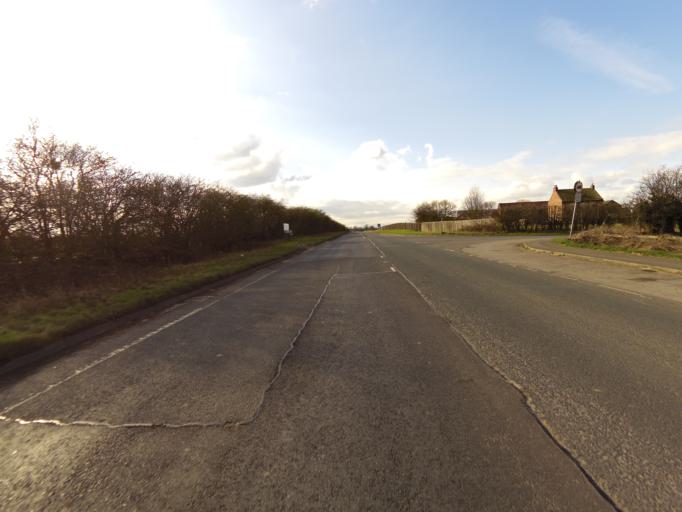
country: GB
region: England
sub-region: East Riding of Yorkshire
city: Pollington
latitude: 53.6823
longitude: -1.0650
